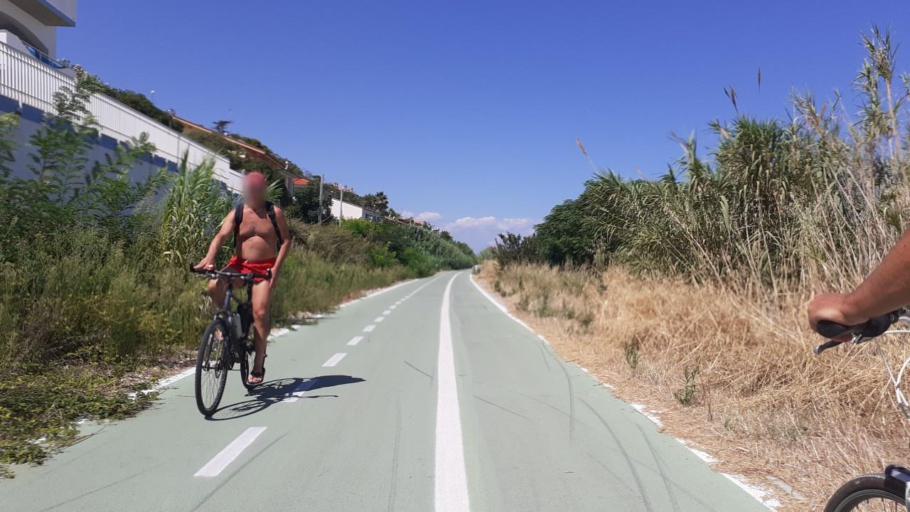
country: IT
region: Abruzzo
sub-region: Provincia di Chieti
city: Villalfonsina
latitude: 42.2079
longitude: 14.5959
